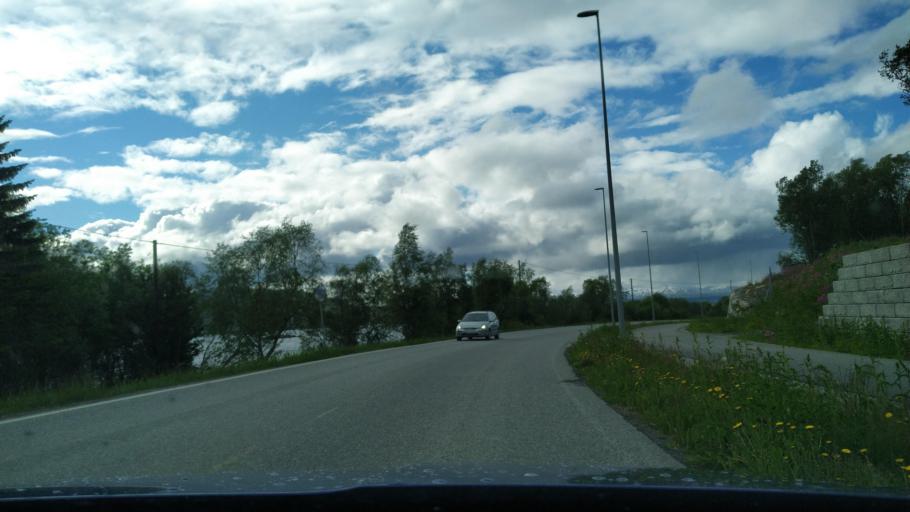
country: NO
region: Troms
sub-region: Lenvik
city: Finnsnes
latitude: 69.1790
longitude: 18.0597
